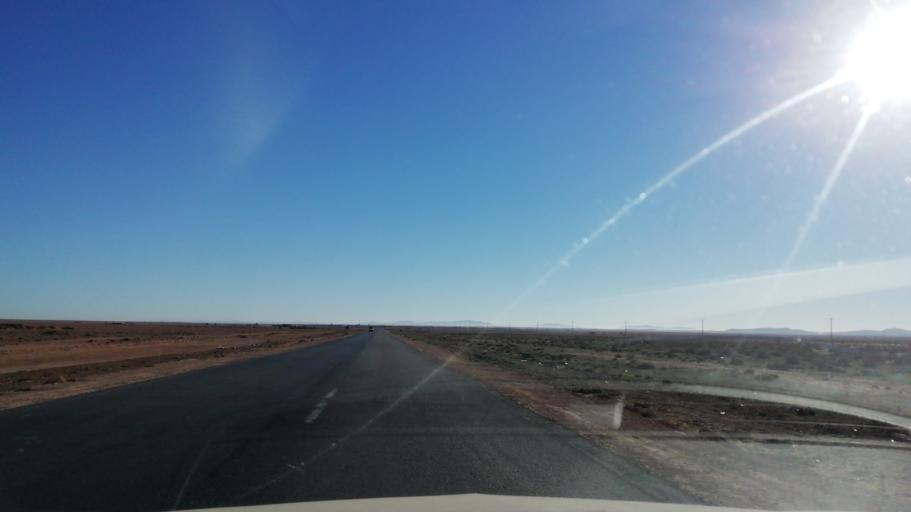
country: DZ
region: El Bayadh
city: El Bayadh
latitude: 33.8567
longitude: 0.5869
